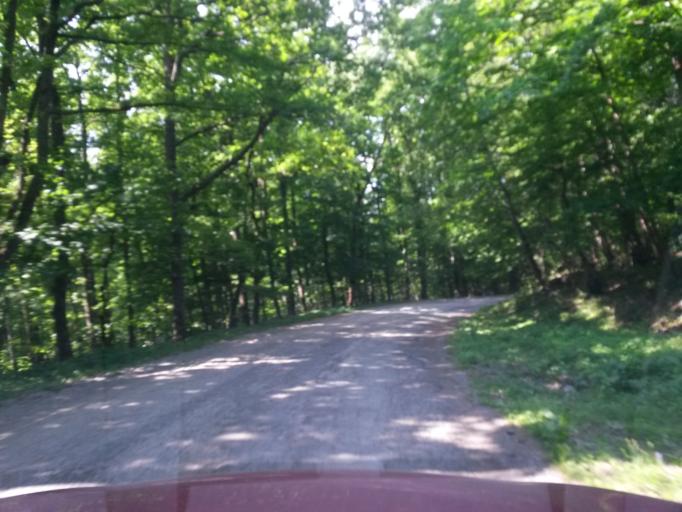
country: SK
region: Kosicky
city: Moldava nad Bodvou
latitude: 48.7166
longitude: 21.0283
